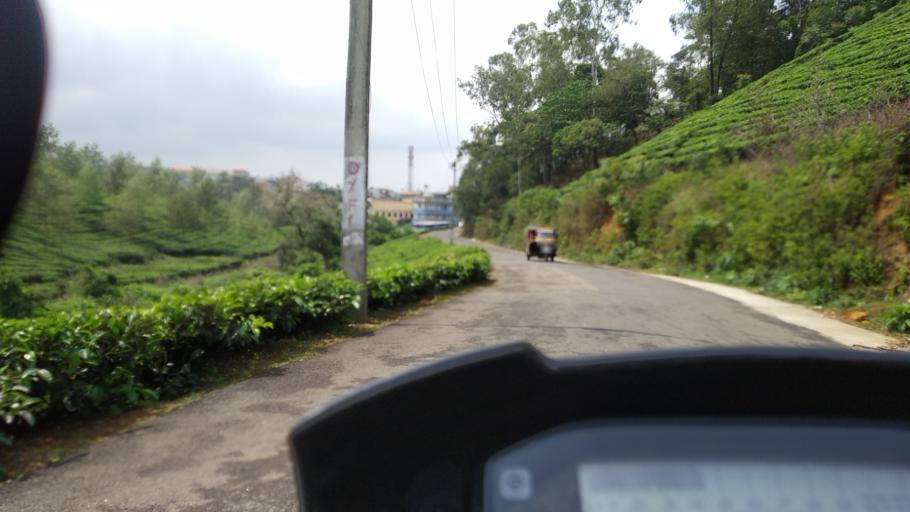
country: IN
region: Kerala
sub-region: Kottayam
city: Erattupetta
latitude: 9.6282
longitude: 76.9772
